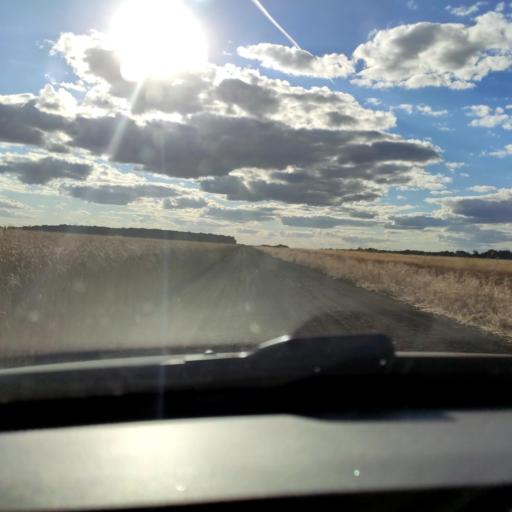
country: RU
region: Voronezj
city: Verkhnyaya Khava
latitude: 51.6088
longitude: 39.8325
